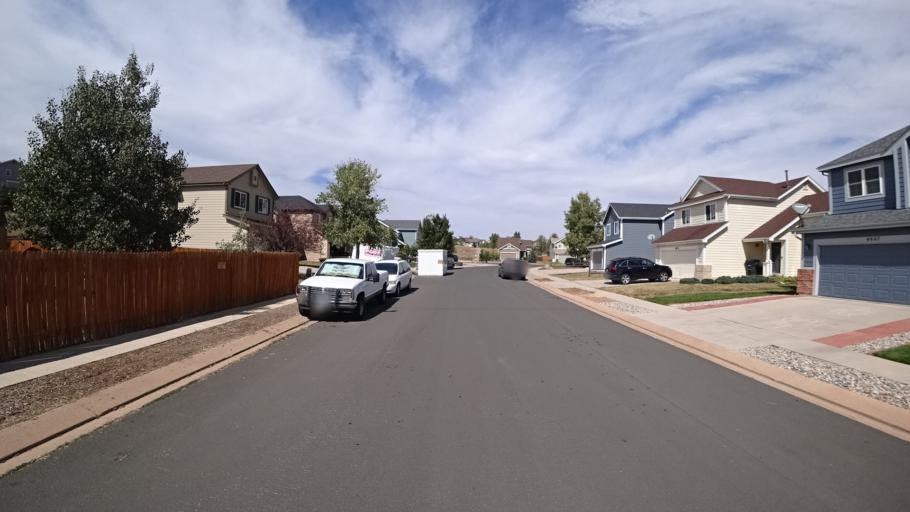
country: US
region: Colorado
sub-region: El Paso County
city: Cimarron Hills
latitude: 38.8998
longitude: -104.7161
